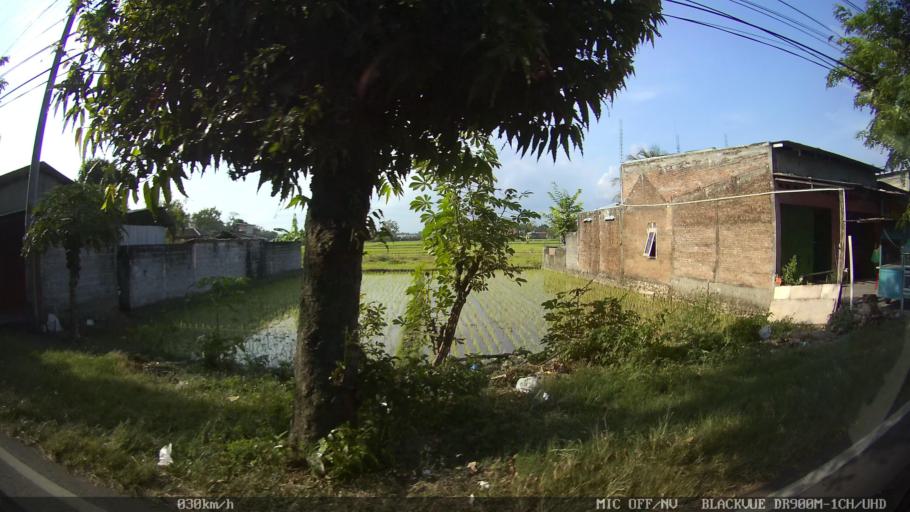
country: ID
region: Daerah Istimewa Yogyakarta
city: Bantul
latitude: -7.8790
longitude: 110.3316
